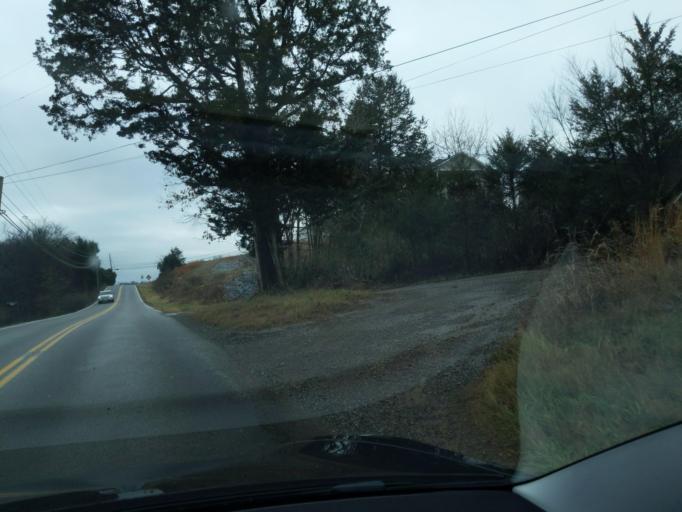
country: US
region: Tennessee
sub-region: Sevier County
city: Sevierville
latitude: 35.9592
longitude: -83.5890
